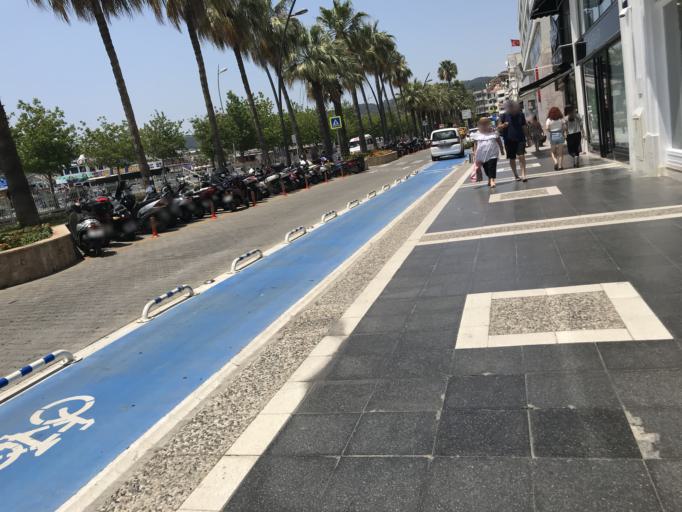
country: TR
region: Mugla
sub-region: Marmaris
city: Marmaris
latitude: 36.8517
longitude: 28.2734
